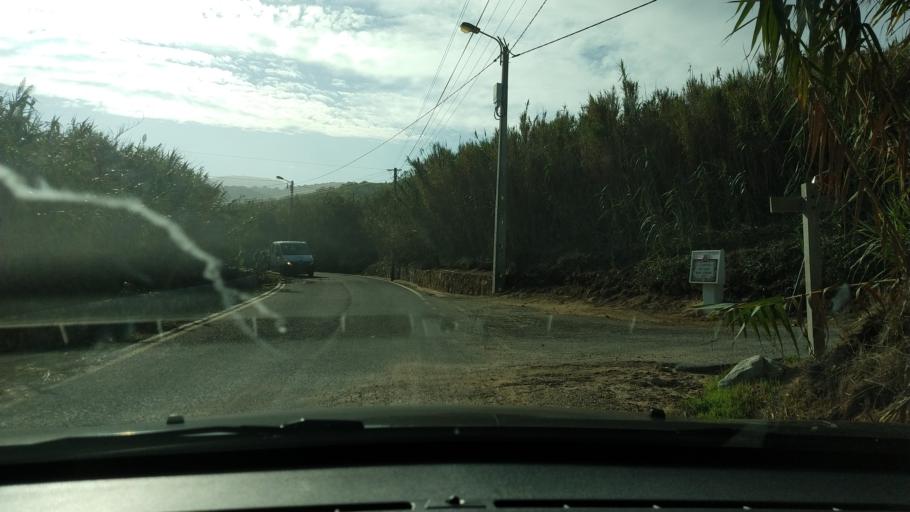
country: PT
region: Lisbon
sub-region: Sintra
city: Colares
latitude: 38.7994
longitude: -9.4843
